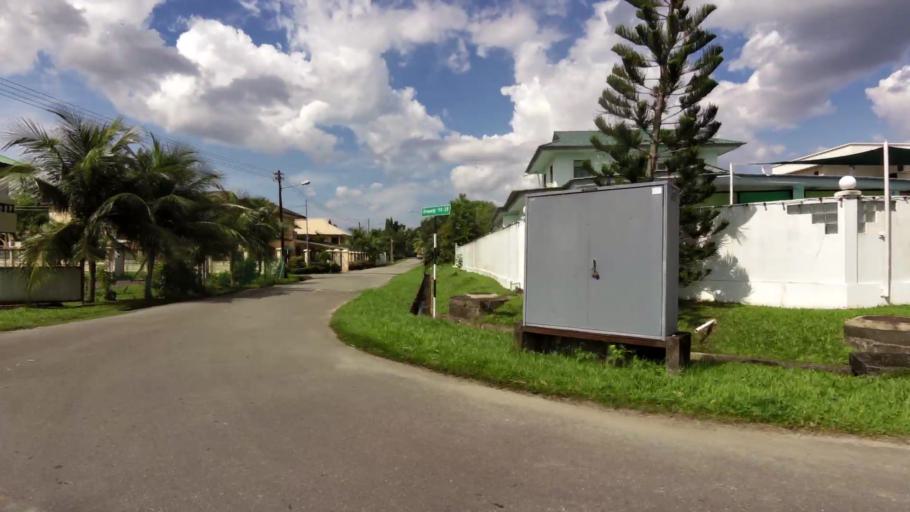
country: BN
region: Brunei and Muara
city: Bandar Seri Begawan
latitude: 4.9579
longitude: 114.9542
